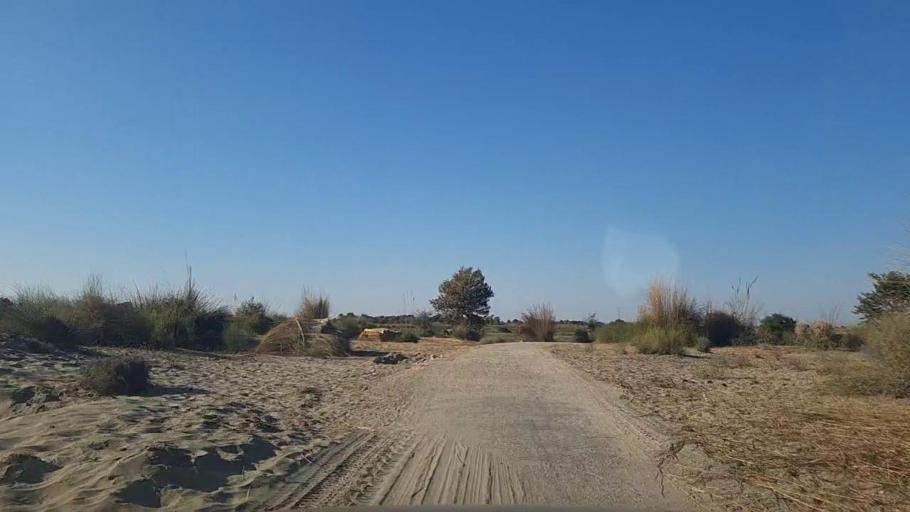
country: PK
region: Sindh
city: Khadro
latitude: 26.2433
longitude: 68.8633
